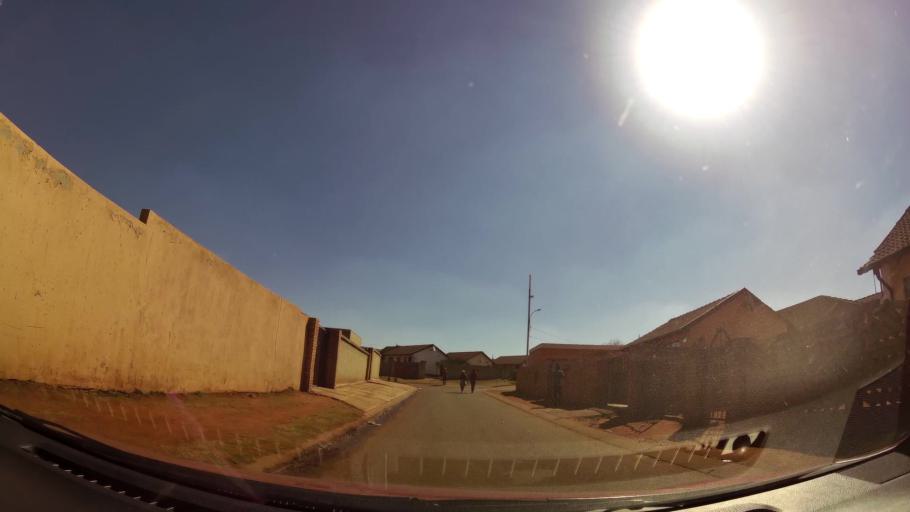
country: ZA
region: Gauteng
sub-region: City of Johannesburg Metropolitan Municipality
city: Soweto
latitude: -26.2478
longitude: 27.8062
